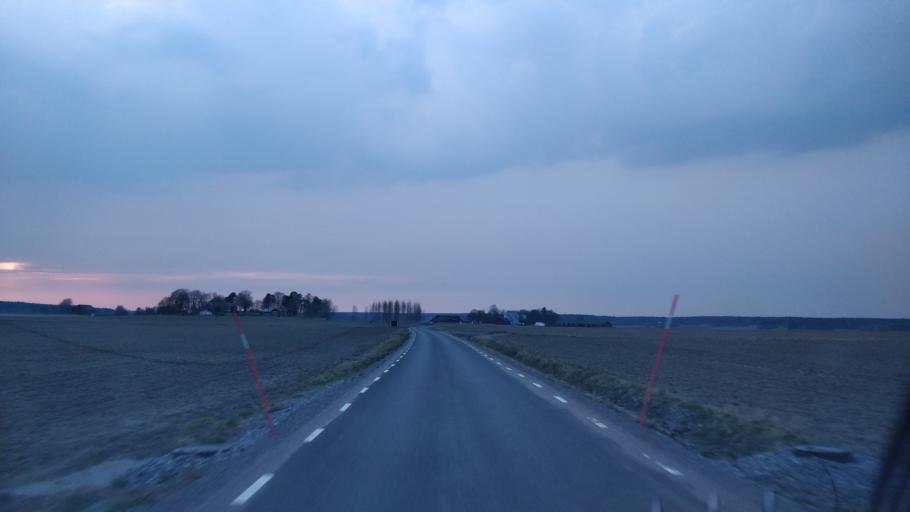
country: SE
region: Uppsala
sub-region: Enkopings Kommun
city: Orsundsbro
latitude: 59.7268
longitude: 17.2172
